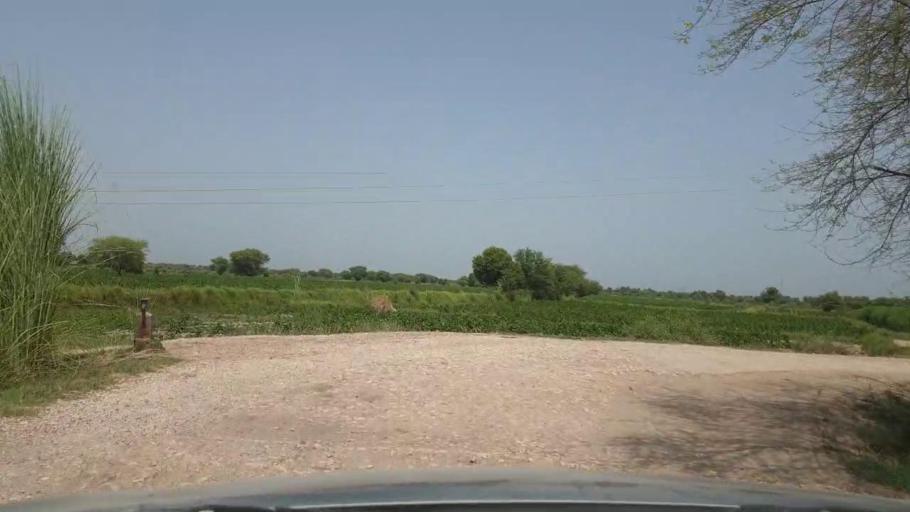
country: PK
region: Sindh
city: Pano Aqil
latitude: 27.8209
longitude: 69.2283
